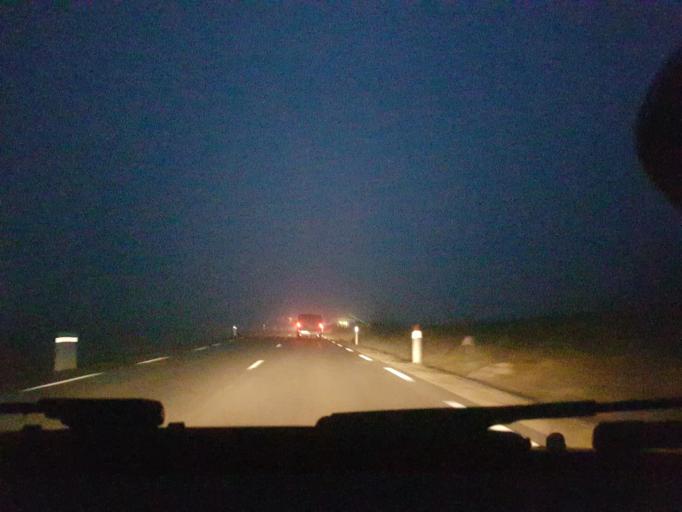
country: FR
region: Franche-Comte
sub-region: Departement du Doubs
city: Doubs
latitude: 46.9745
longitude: 6.3434
